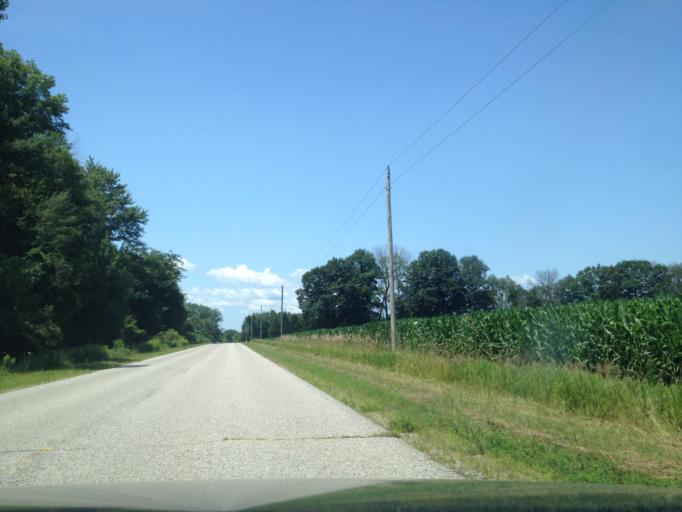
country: CA
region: Ontario
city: Aylmer
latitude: 42.6432
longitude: -80.7835
